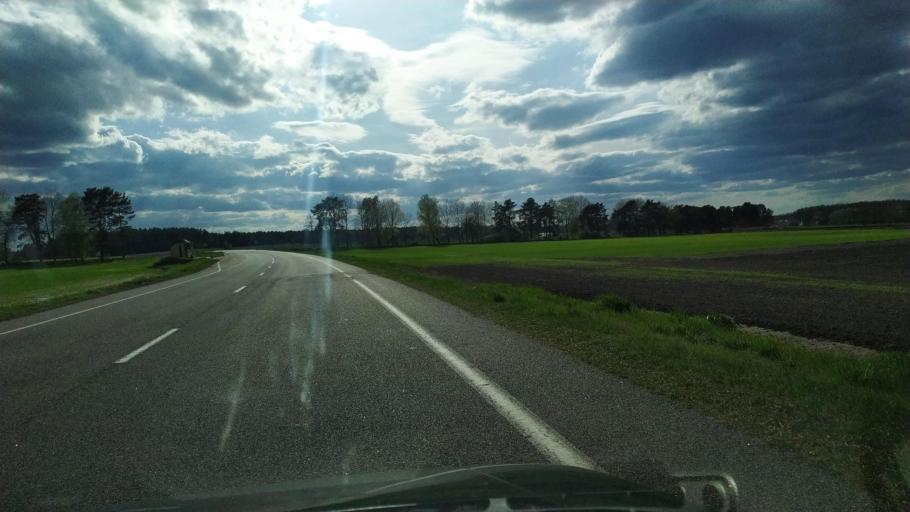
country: BY
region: Brest
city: Pruzhany
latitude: 52.6962
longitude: 24.2245
